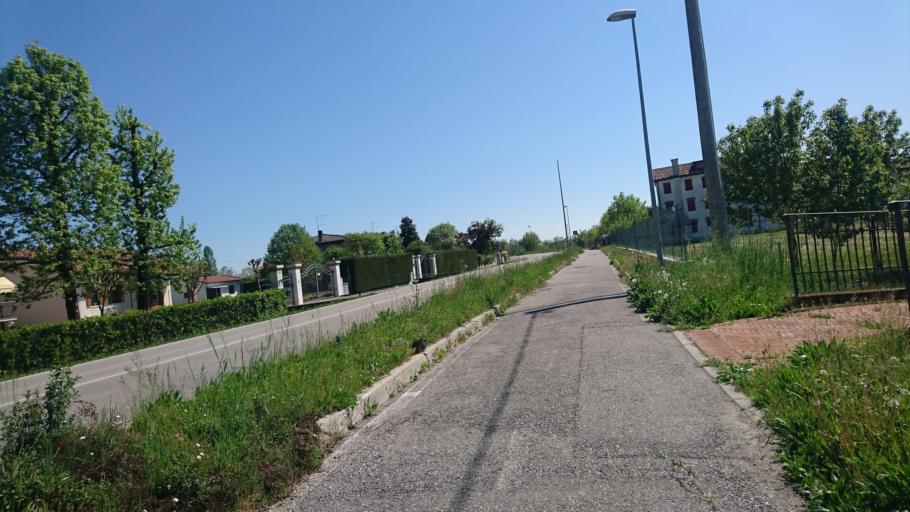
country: IT
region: Veneto
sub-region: Provincia di Treviso
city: Conscio
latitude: 45.6064
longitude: 12.2847
